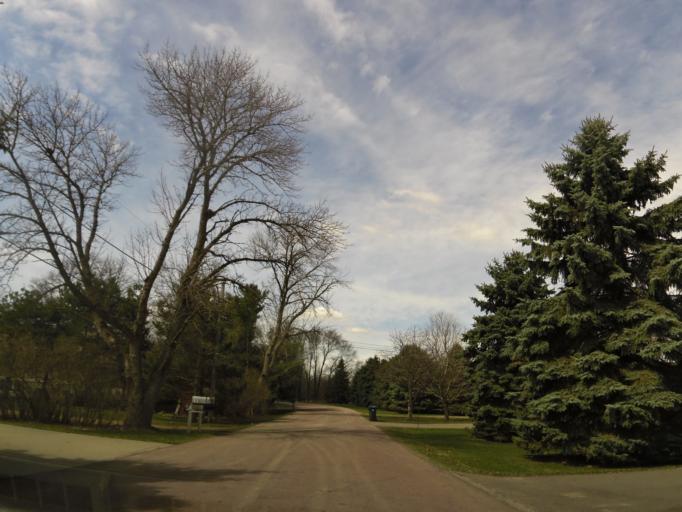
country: US
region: Minnesota
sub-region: Goodhue County
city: Cannon Falls
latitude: 44.5191
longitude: -92.9539
